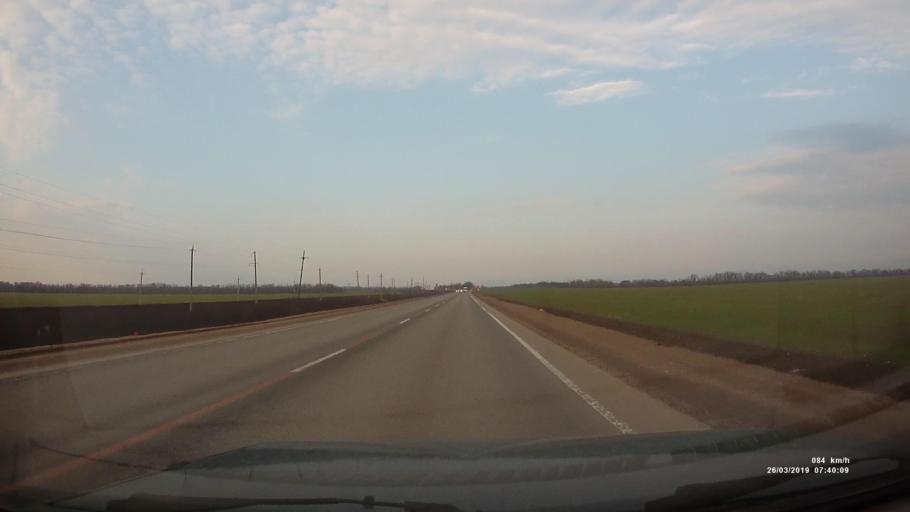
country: RU
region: Rostov
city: Novobessergenovka
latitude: 47.1953
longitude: 38.6534
